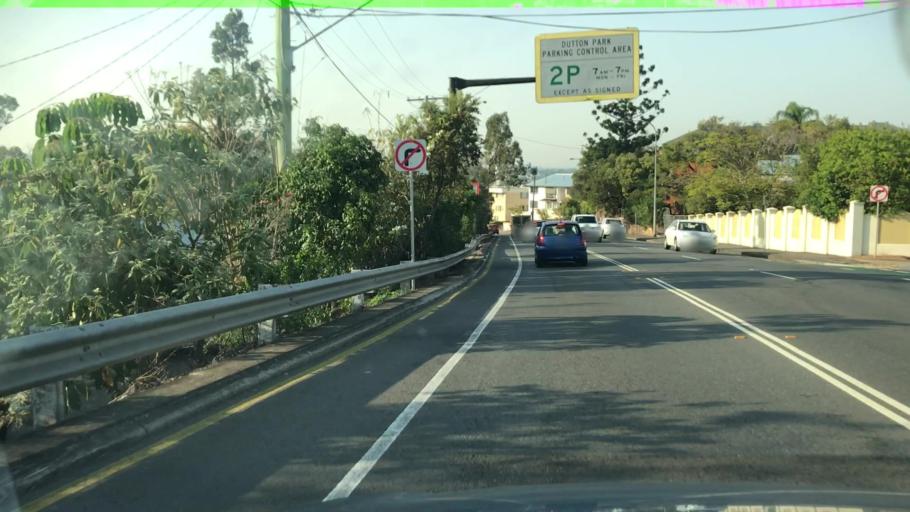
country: AU
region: Queensland
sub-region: Brisbane
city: South Brisbane
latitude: -27.4892
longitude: 153.0186
